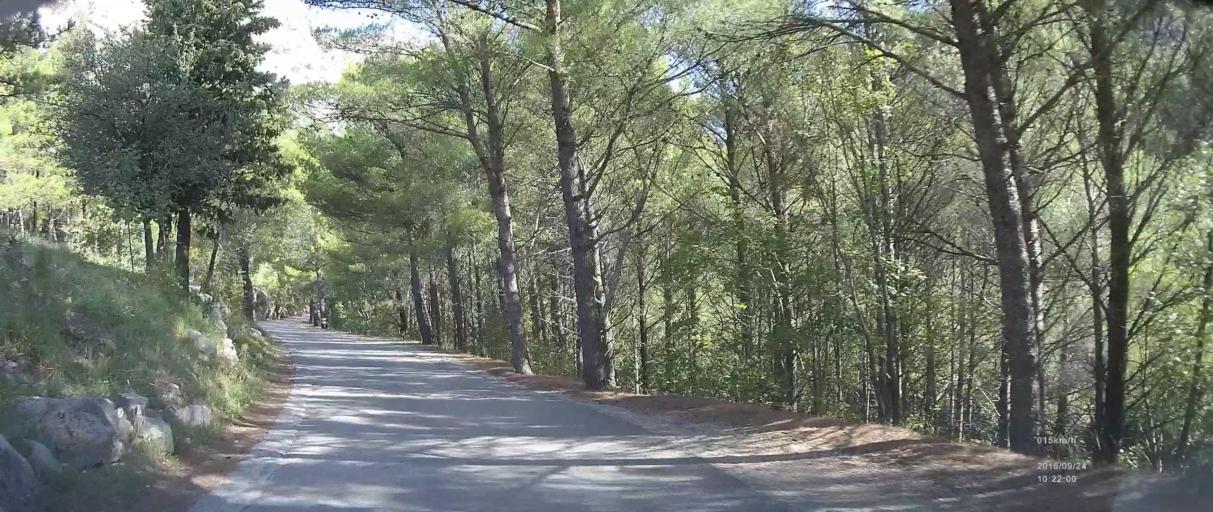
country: HR
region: Zadarska
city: Starigrad
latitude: 44.2961
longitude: 15.4601
